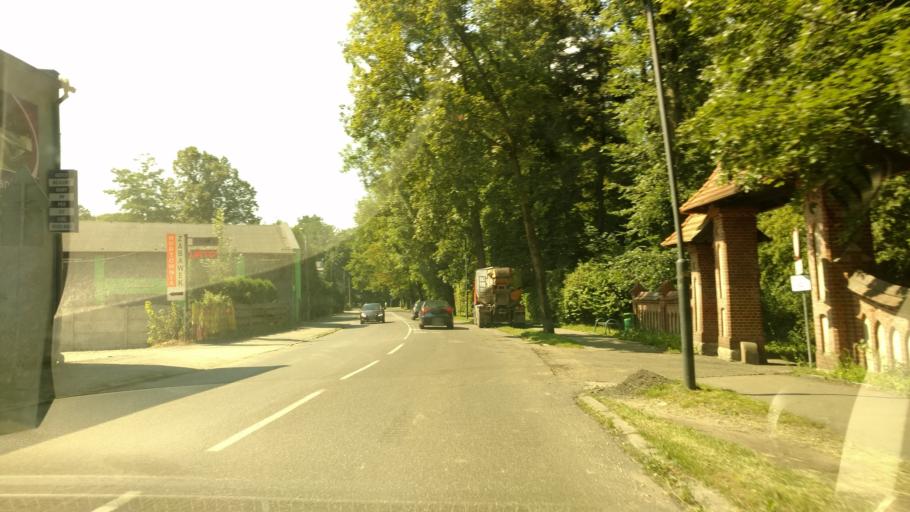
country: PL
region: Silesian Voivodeship
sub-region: Powiat pszczynski
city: Pszczyna
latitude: 49.9825
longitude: 18.9467
